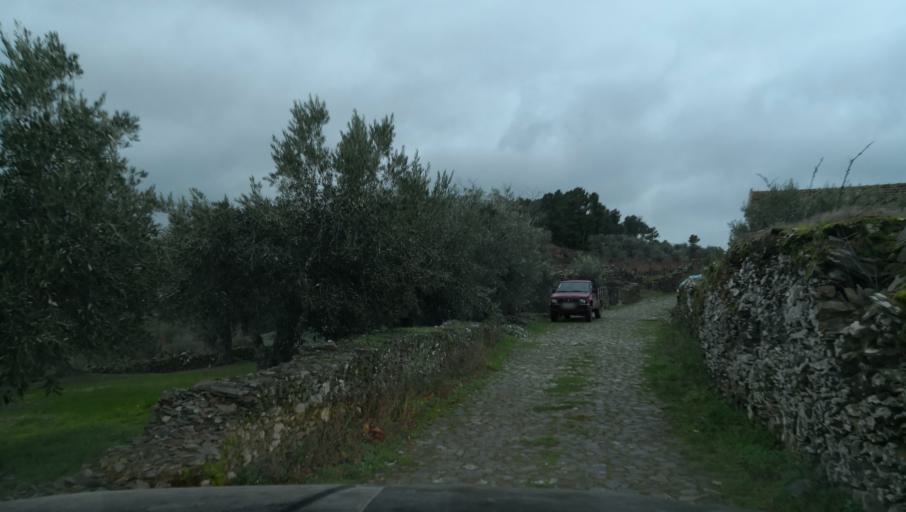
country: PT
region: Vila Real
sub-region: Vila Real
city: Vila Real
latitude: 41.2487
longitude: -7.7390
